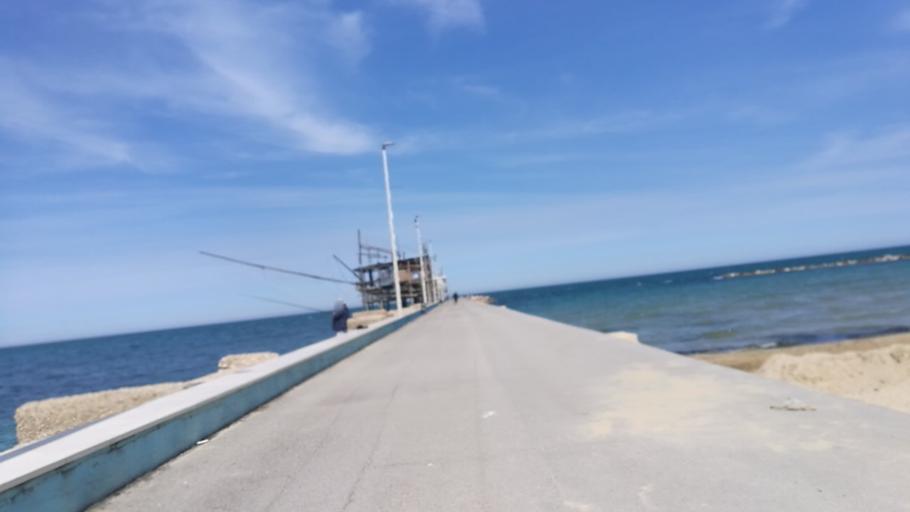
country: IT
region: Abruzzo
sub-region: Provincia di Chieti
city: Marina di San Vito
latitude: 42.3091
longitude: 14.4449
